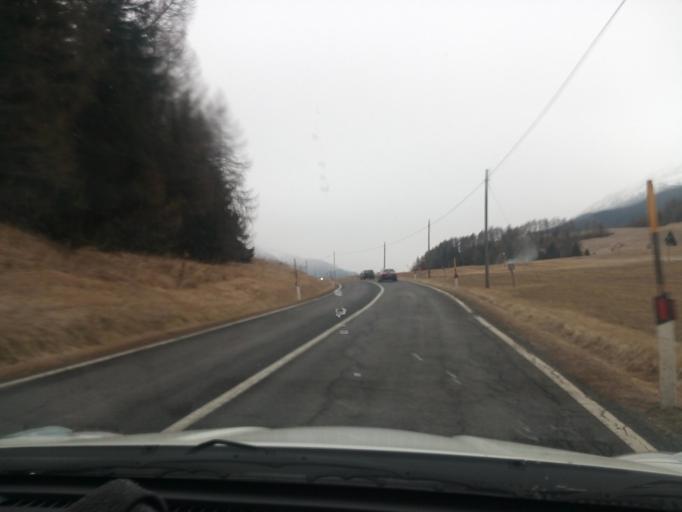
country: IT
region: Trentino-Alto Adige
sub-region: Bolzano
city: Curon Venosta
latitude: 46.8367
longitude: 10.5084
